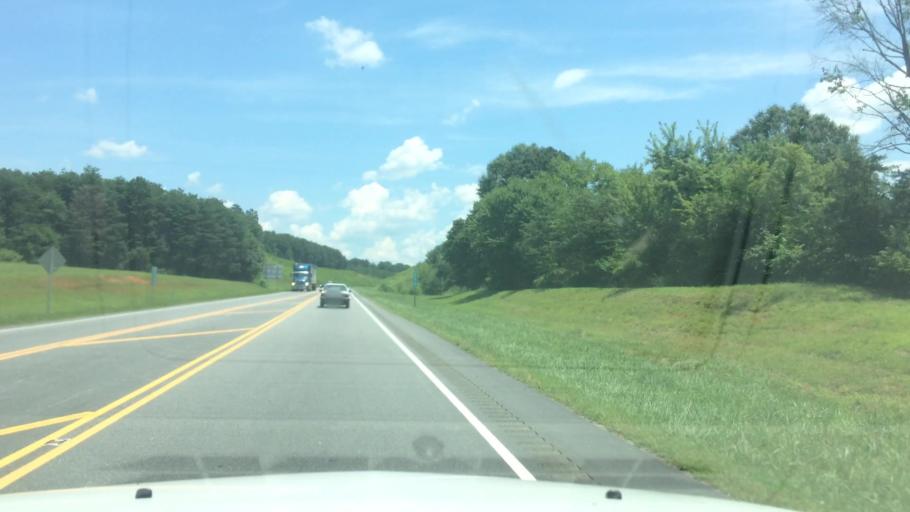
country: US
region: North Carolina
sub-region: Alexander County
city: Taylorsville
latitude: 35.9110
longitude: -81.1560
